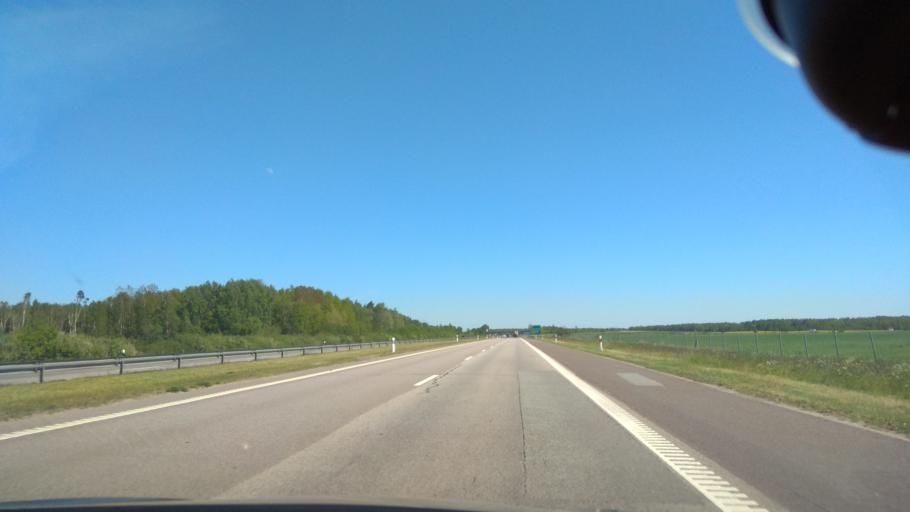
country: LT
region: Klaipedos apskritis
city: Gargzdai
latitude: 55.7208
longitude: 21.4351
